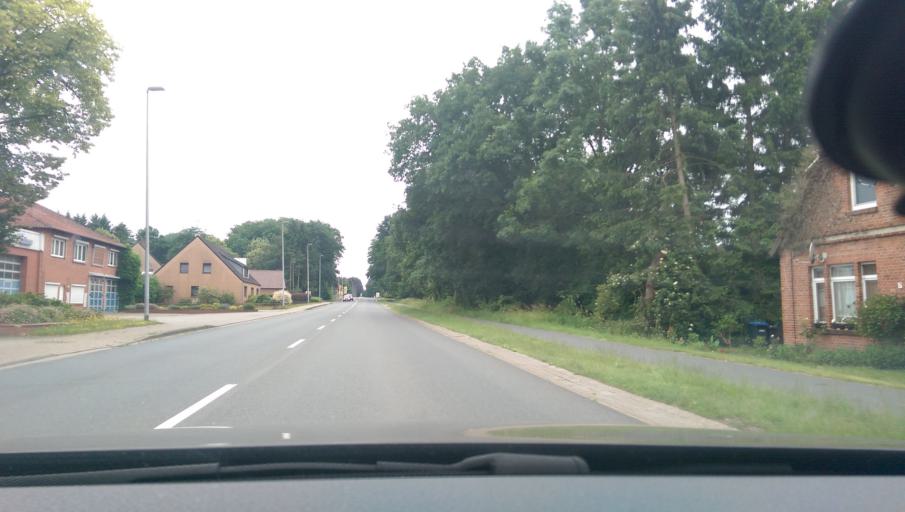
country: DE
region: Lower Saxony
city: Ahausen
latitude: 53.0802
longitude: 9.3573
